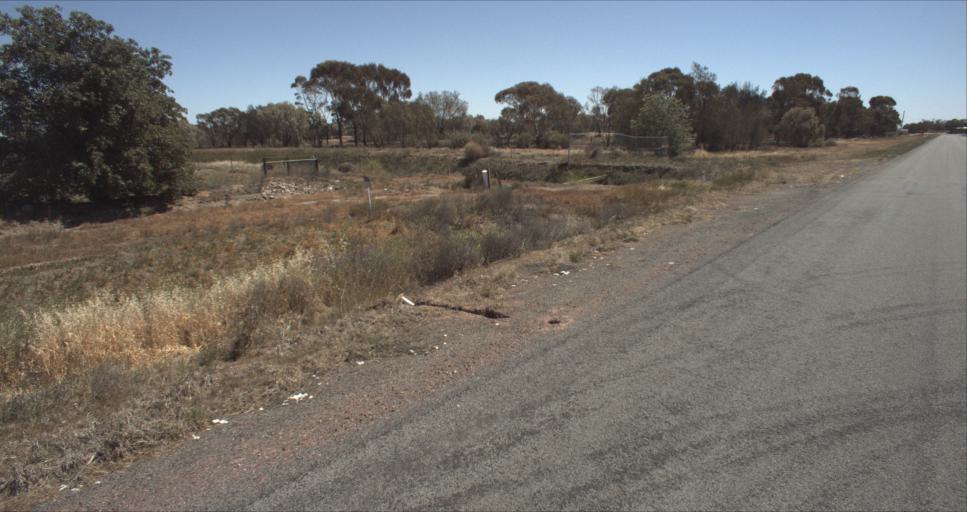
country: AU
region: New South Wales
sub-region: Leeton
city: Leeton
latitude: -34.4314
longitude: 146.2996
